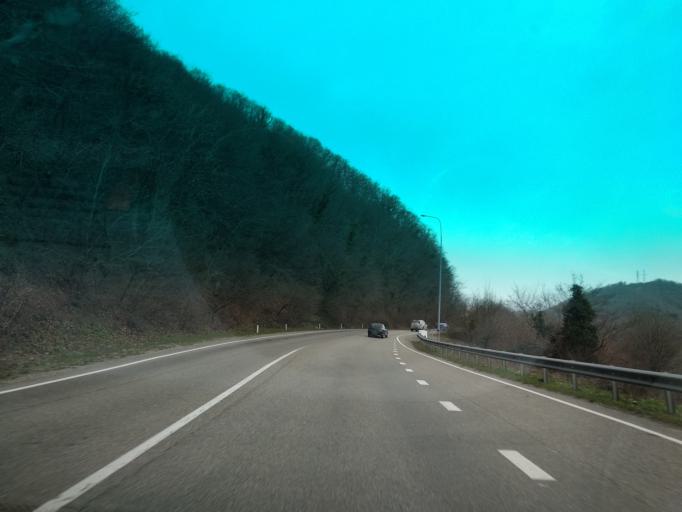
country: RU
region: Krasnodarskiy
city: Ol'ginka
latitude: 44.2197
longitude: 38.8943
